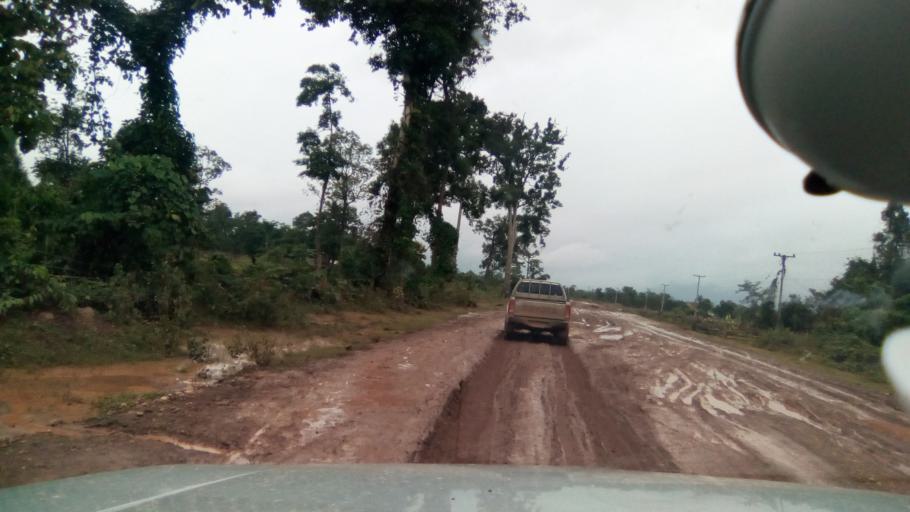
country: LA
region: Attapu
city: Attapu
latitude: 14.6861
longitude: 106.5482
